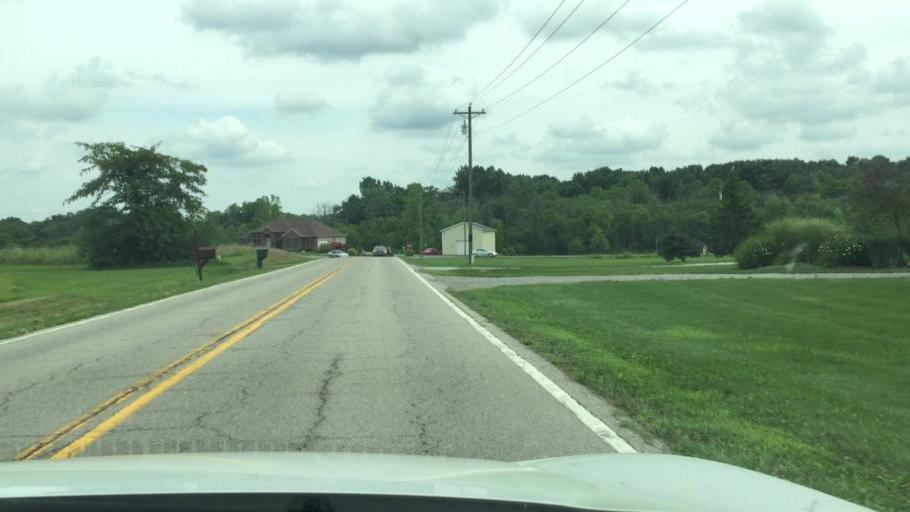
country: US
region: Ohio
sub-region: Union County
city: Marysville
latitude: 40.2255
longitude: -83.4581
